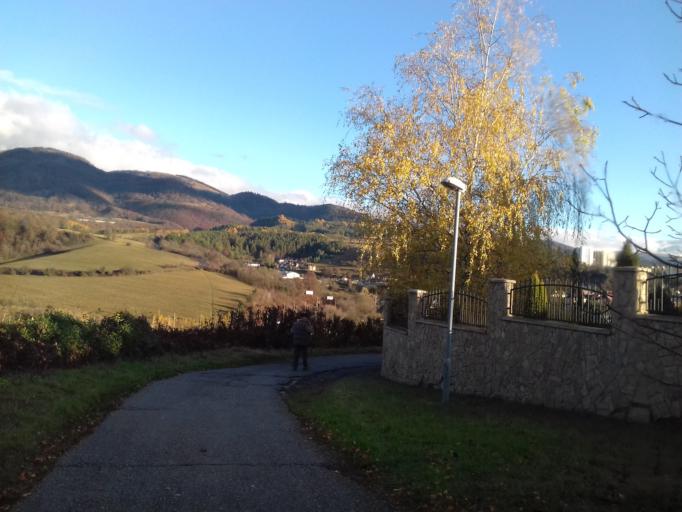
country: SK
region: Banskobystricky
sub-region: Okres Banska Bystrica
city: Banska Bystrica
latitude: 48.7536
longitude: 19.1500
